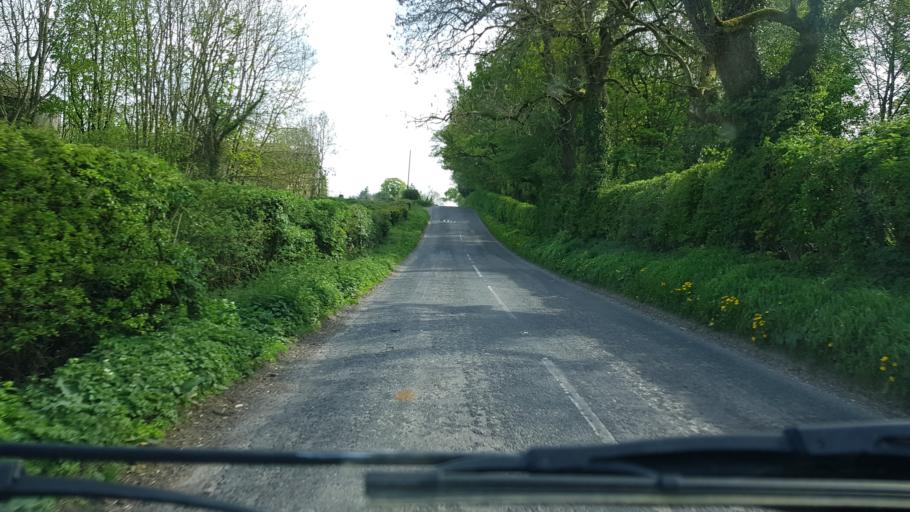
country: GB
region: England
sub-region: Hampshire
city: Overton
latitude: 51.2761
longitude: -1.2631
